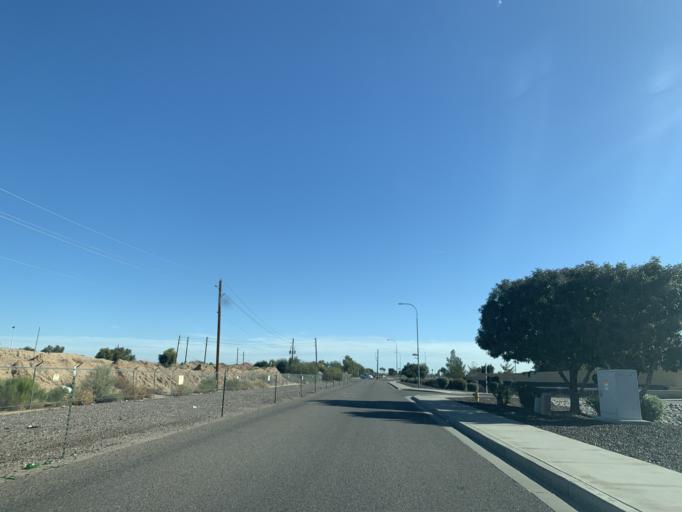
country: US
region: Arizona
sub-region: Maricopa County
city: Laveen
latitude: 33.3994
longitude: -112.1186
